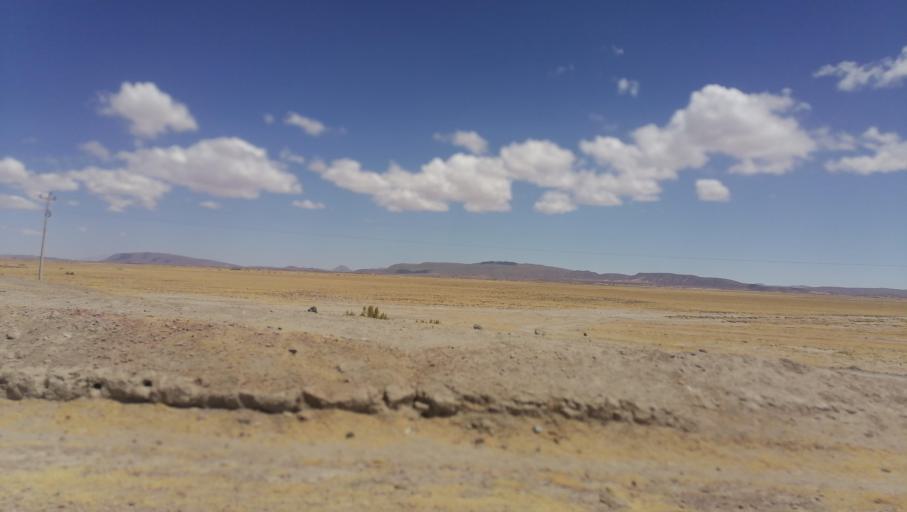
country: BO
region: Oruro
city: Challapata
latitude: -19.2190
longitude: -66.9993
